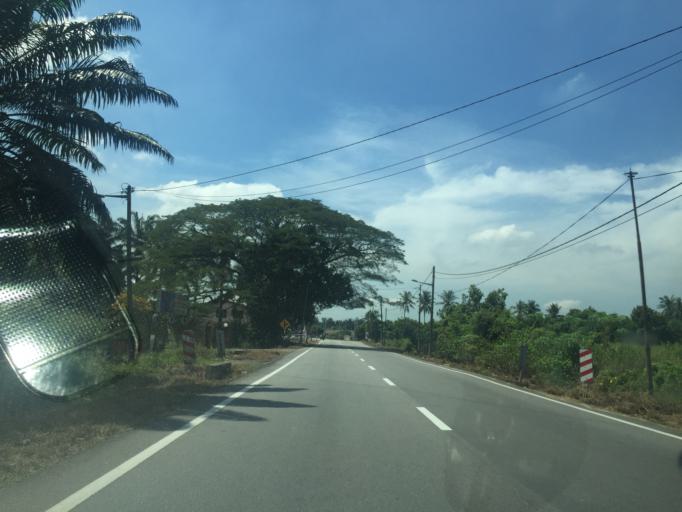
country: MY
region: Penang
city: Tasek Glugor
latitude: 5.4882
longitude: 100.5050
